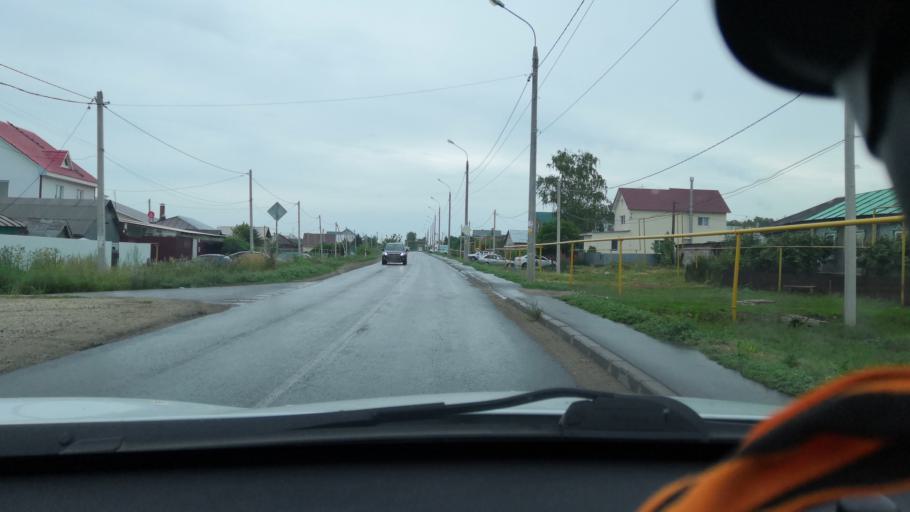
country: RU
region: Samara
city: Novosemeykino
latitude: 53.3795
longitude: 50.3500
